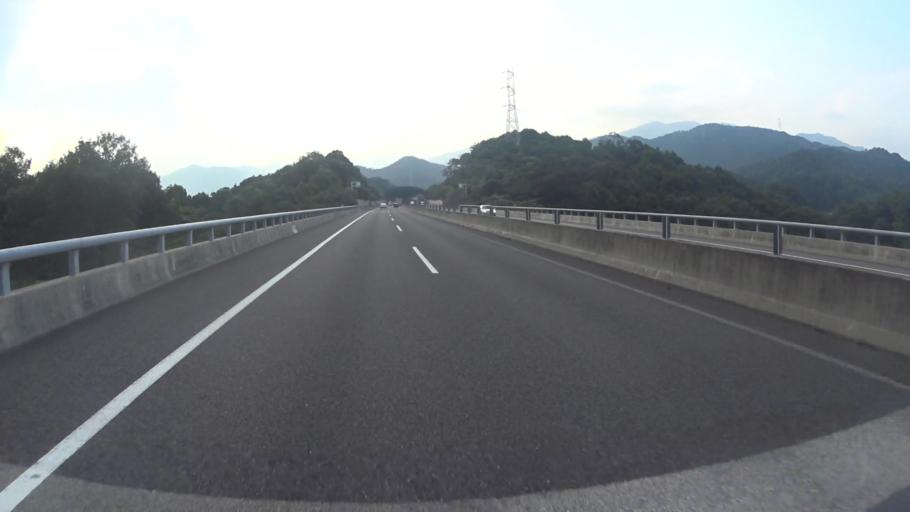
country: JP
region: Mie
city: Kameyama
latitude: 34.9061
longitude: 136.4352
